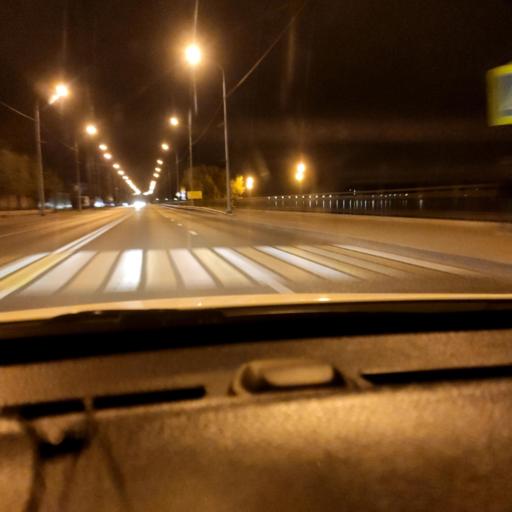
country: RU
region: Voronezj
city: Voronezh
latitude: 51.6726
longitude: 39.2243
